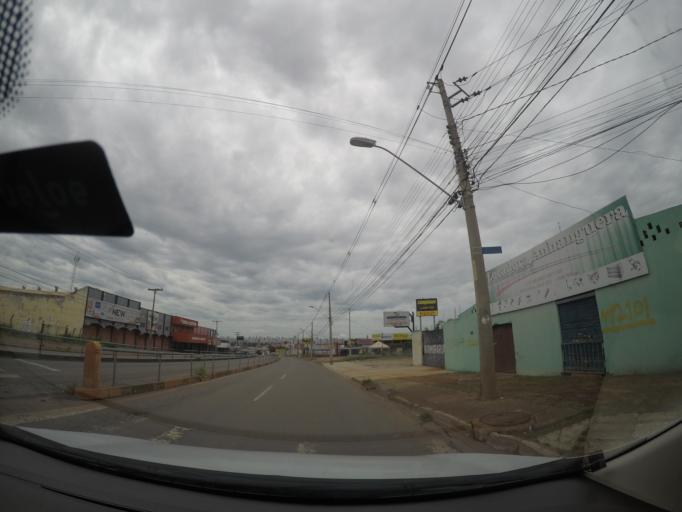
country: BR
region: Goias
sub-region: Goiania
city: Goiania
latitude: -16.6632
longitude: -49.3225
